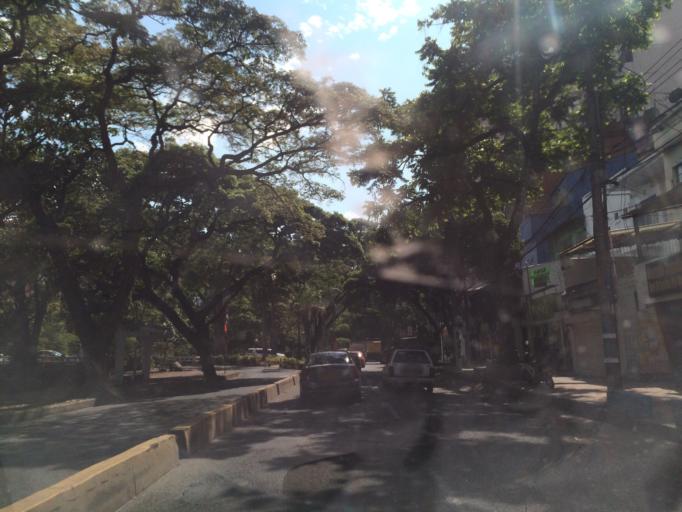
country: CO
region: Valle del Cauca
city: Cali
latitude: 3.4517
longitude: -76.5422
